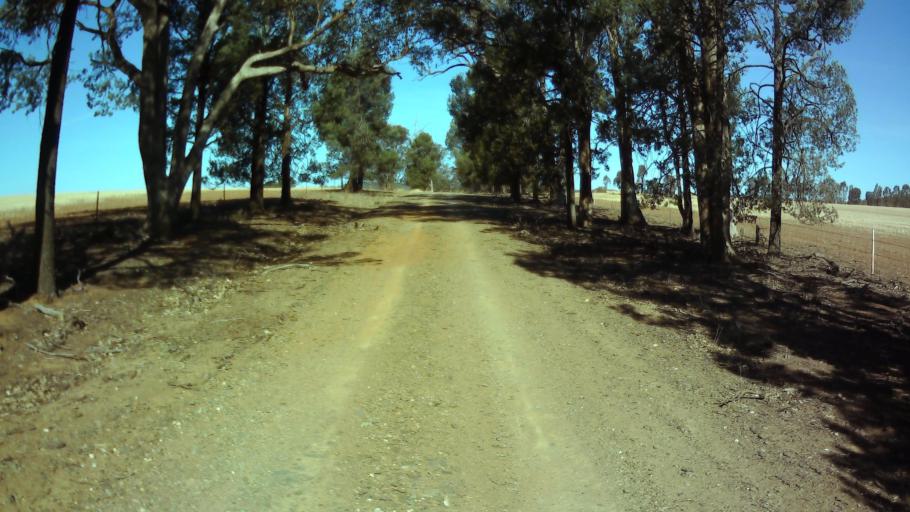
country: AU
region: New South Wales
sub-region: Weddin
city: Grenfell
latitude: -33.7797
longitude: 147.8322
